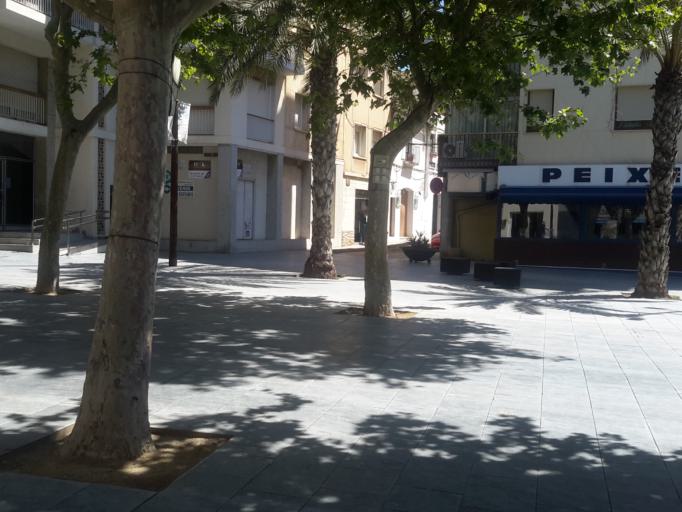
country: ES
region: Catalonia
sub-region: Provincia de Barcelona
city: Vilanova i la Geltru
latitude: 41.2158
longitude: 1.7293
